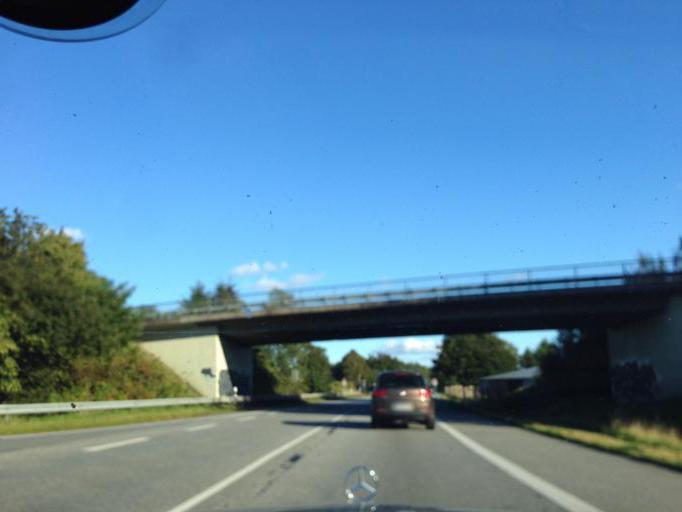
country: DE
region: Schleswig-Holstein
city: Rickling
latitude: 54.0149
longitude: 10.1642
